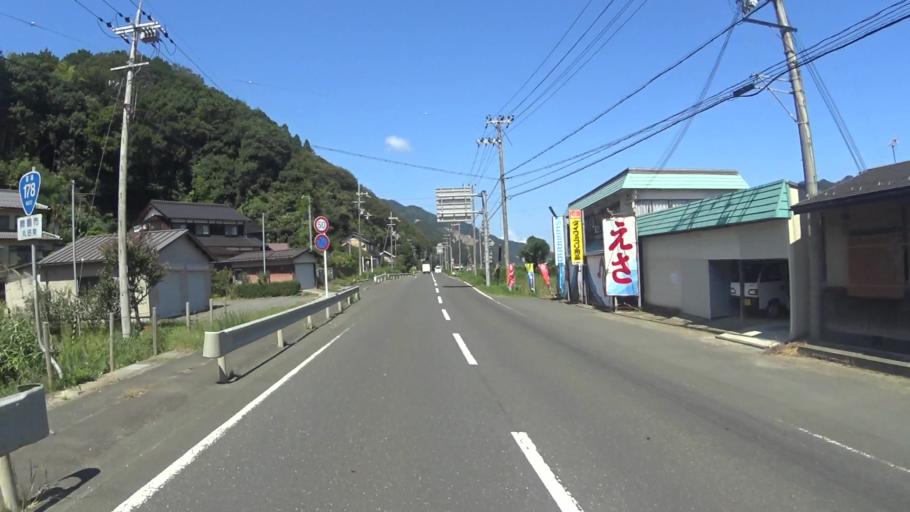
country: JP
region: Kyoto
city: Maizuru
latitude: 35.4660
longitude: 135.2782
